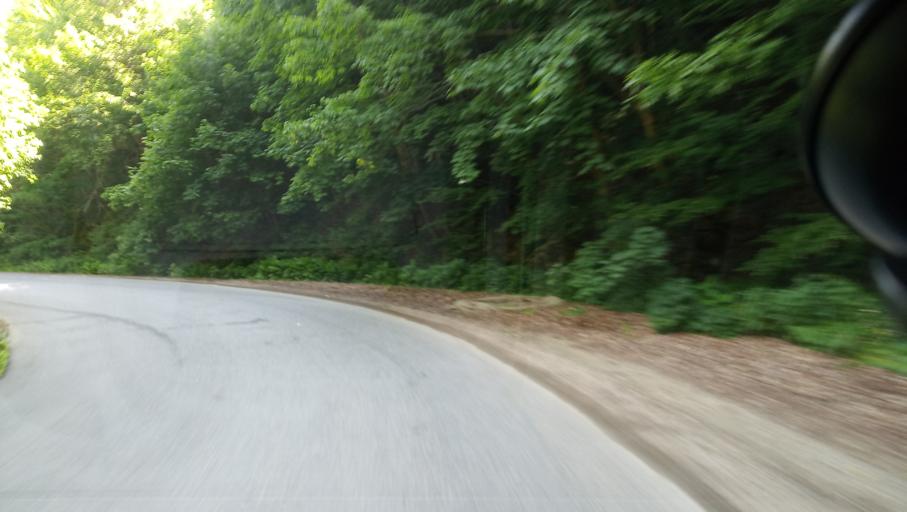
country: RO
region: Cluj
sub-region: Comuna Capusu Mare
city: Capusu Mare
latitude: 46.7259
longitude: 23.2880
